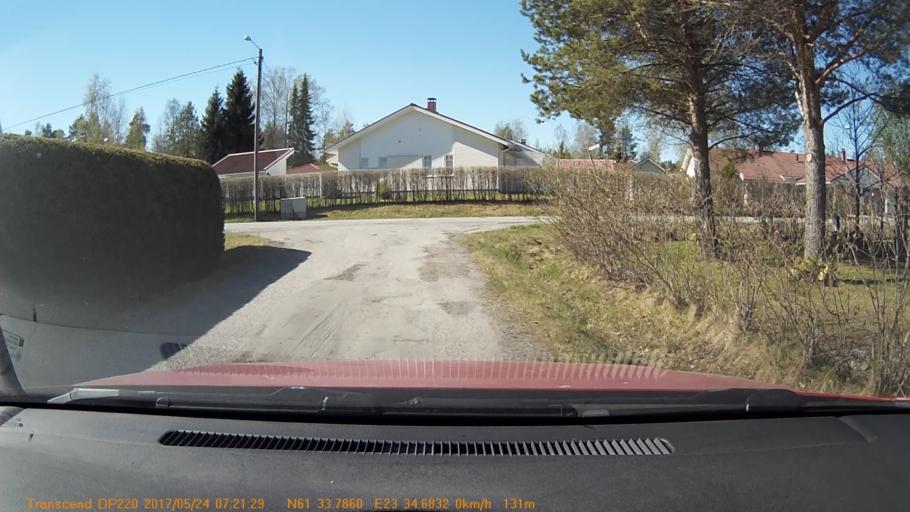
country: FI
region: Pirkanmaa
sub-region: Tampere
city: Yloejaervi
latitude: 61.5631
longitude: 23.5781
